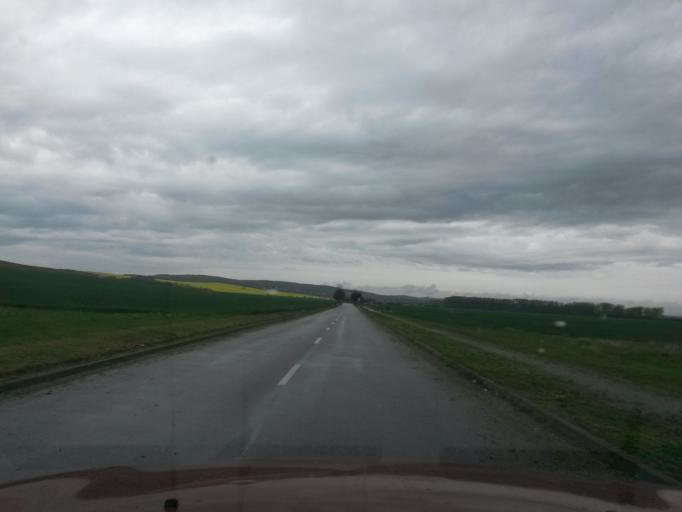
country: HU
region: Borsod-Abauj-Zemplen
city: Gonc
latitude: 48.5473
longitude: 21.2259
